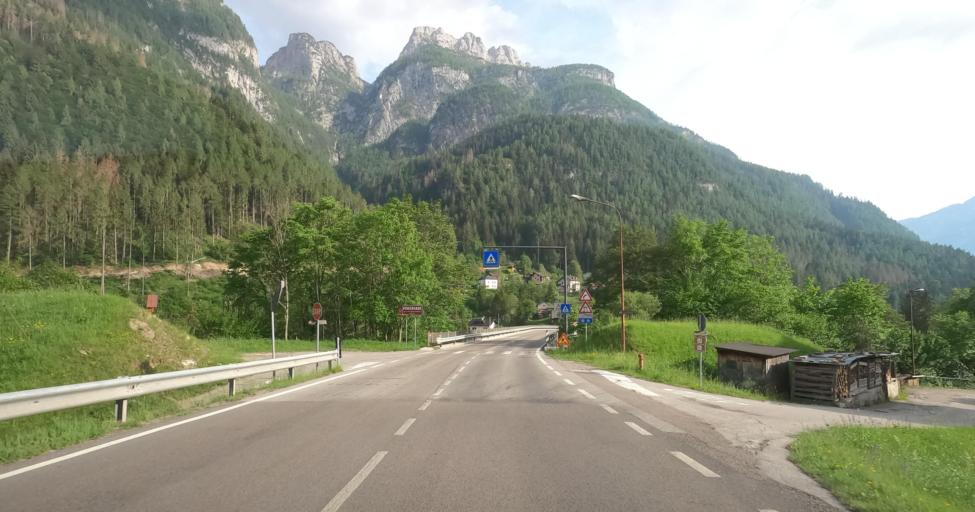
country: IT
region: Veneto
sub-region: Provincia di Belluno
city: Celat-San Tomaso Agordino
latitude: 46.3890
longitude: 11.9987
